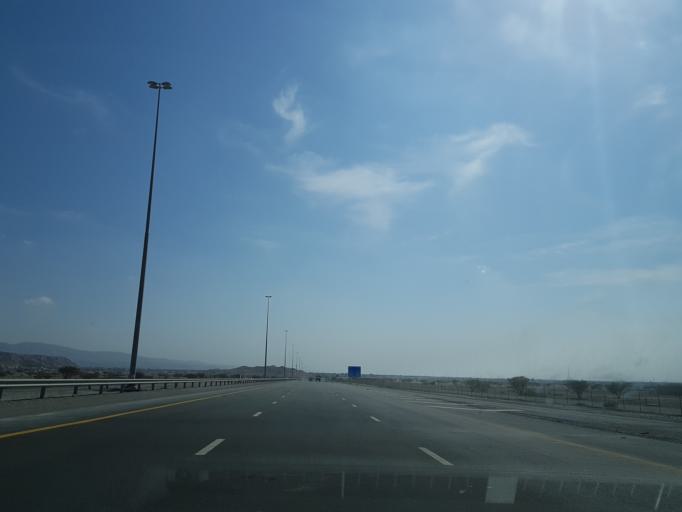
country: AE
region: Ra's al Khaymah
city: Ras al-Khaimah
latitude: 25.7461
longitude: 56.0161
